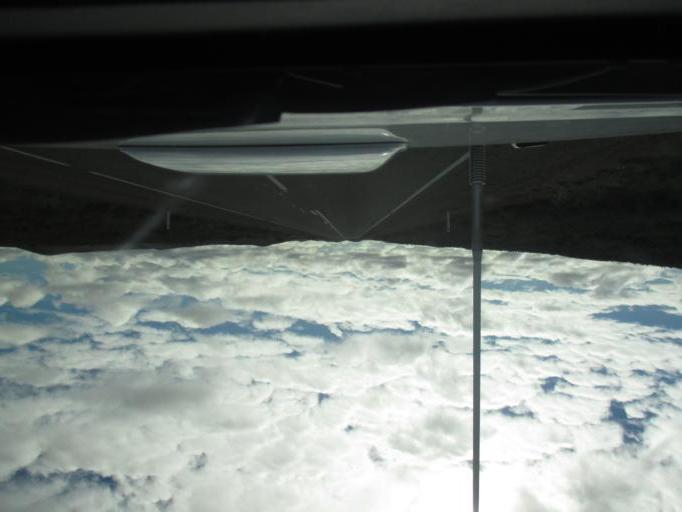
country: AU
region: South Australia
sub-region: Flinders Ranges
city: Quorn
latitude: -32.2582
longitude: 138.5075
